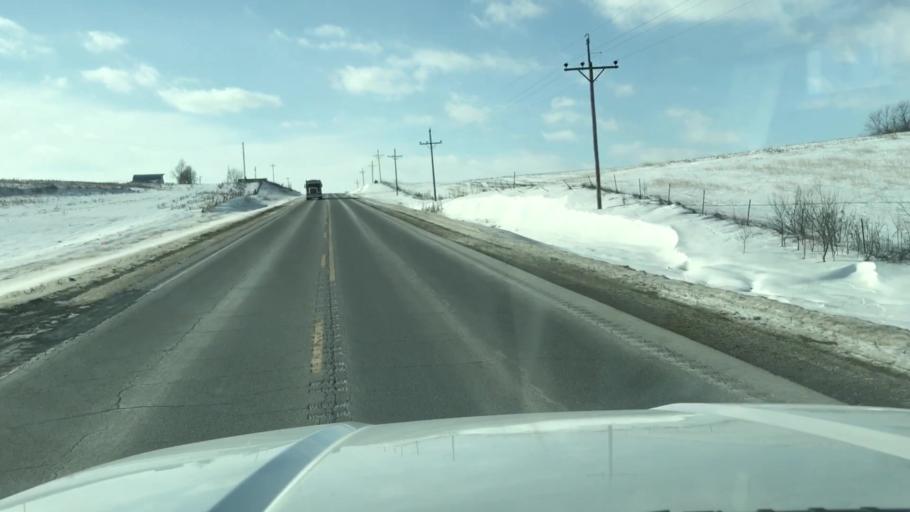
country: US
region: Missouri
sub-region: Nodaway County
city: Maryville
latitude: 40.3441
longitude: -94.7468
